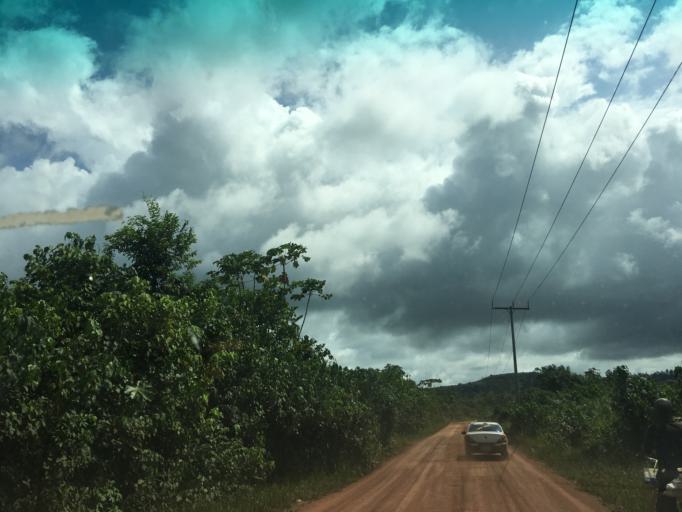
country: GH
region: Western
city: Wassa-Akropong
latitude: 5.7759
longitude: -2.4153
